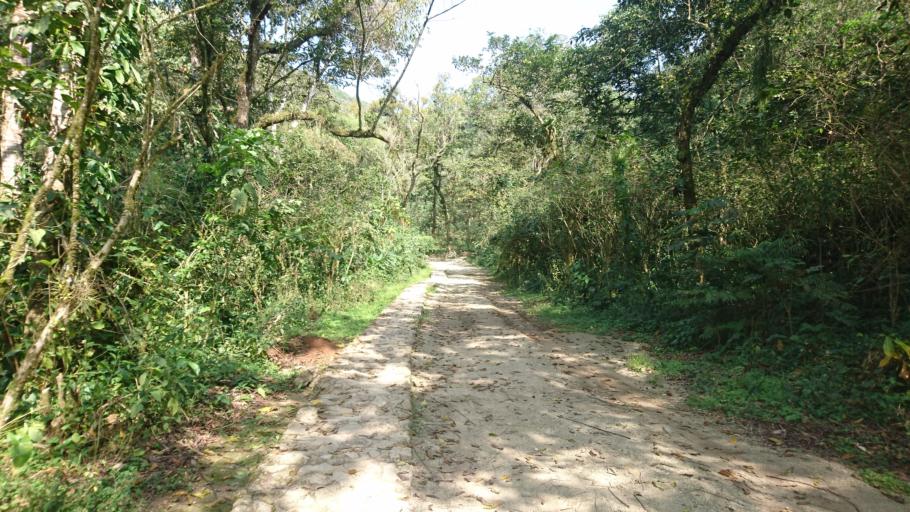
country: MX
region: San Luis Potosi
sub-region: Aquismon
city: Tamapatz
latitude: 21.5255
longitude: -99.0328
